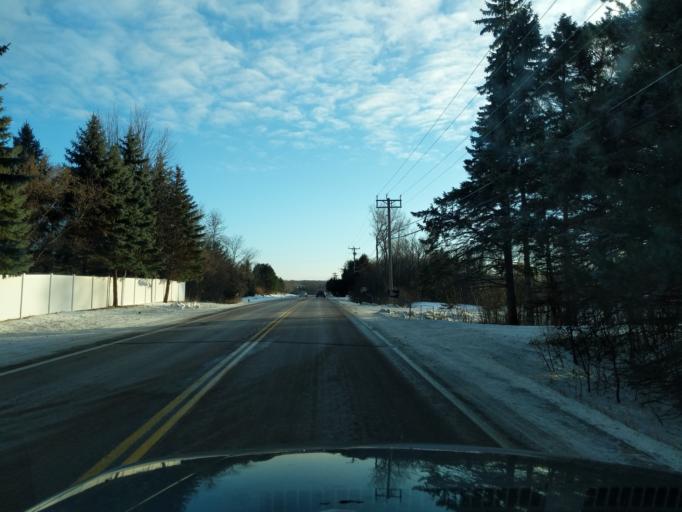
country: US
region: Minnesota
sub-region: Carver County
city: Victoria
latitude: 44.8792
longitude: -93.6415
